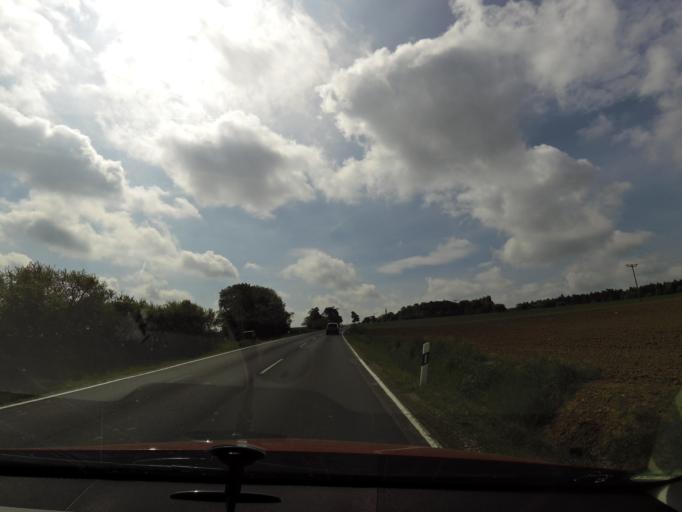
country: DE
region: Thuringia
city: Lauterbach
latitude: 51.0523
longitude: 10.3217
